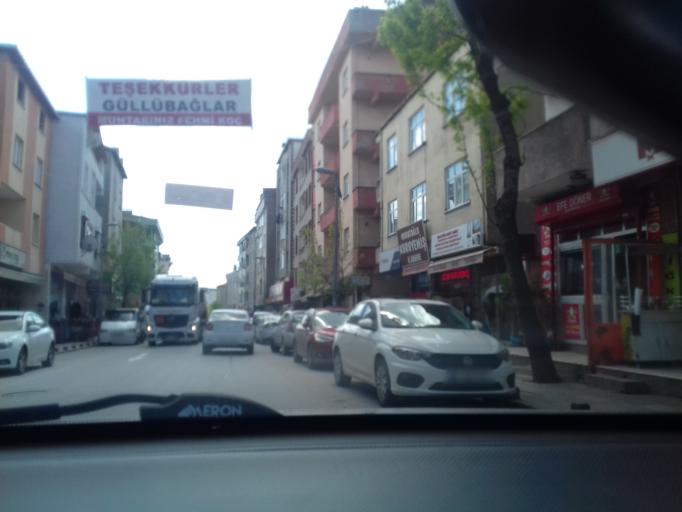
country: TR
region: Istanbul
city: Pendik
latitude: 40.8962
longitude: 29.2747
